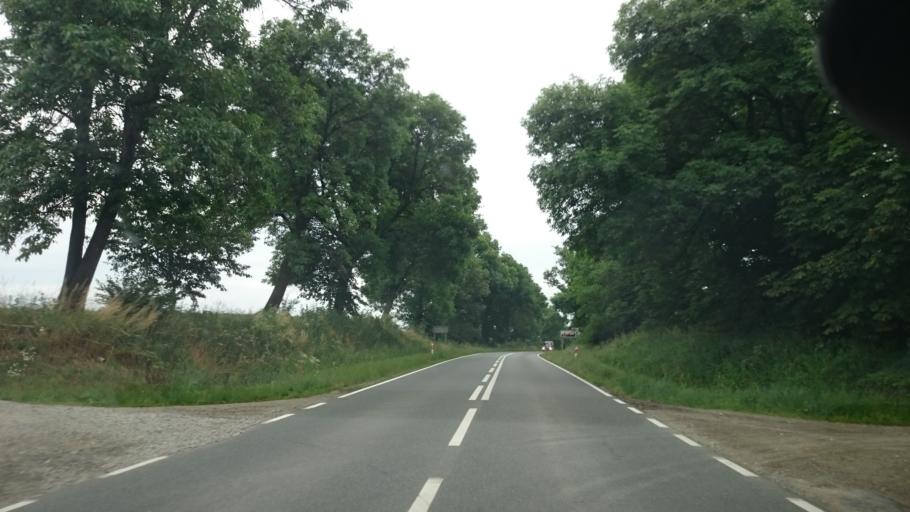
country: PL
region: Lower Silesian Voivodeship
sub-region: Powiat zabkowicki
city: Kamieniec Zabkowicki
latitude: 50.5848
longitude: 16.8863
